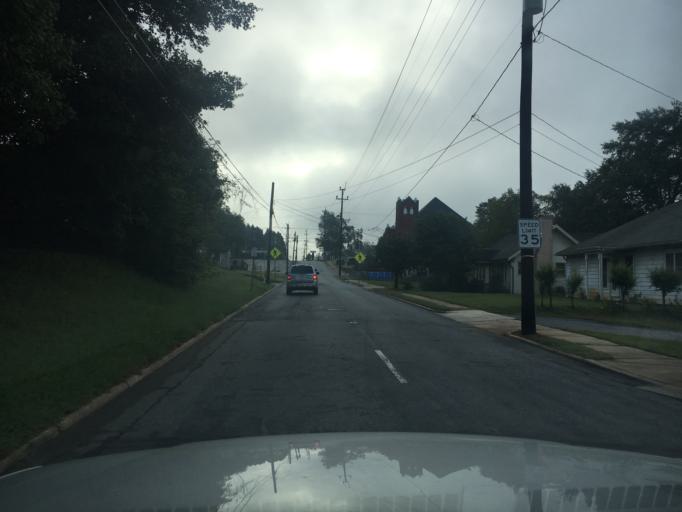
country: US
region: North Carolina
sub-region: Catawba County
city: Hickory
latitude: 35.7300
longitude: -81.3498
